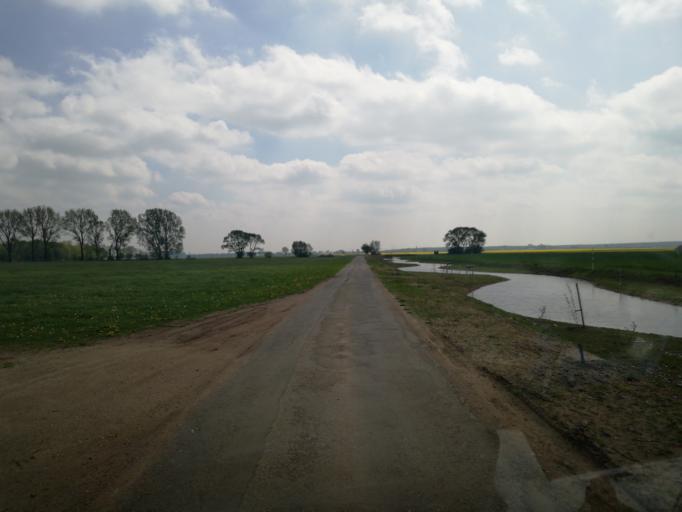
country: DE
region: Brandenburg
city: Doberlug-Kirchhain
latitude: 51.6782
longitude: 13.5362
